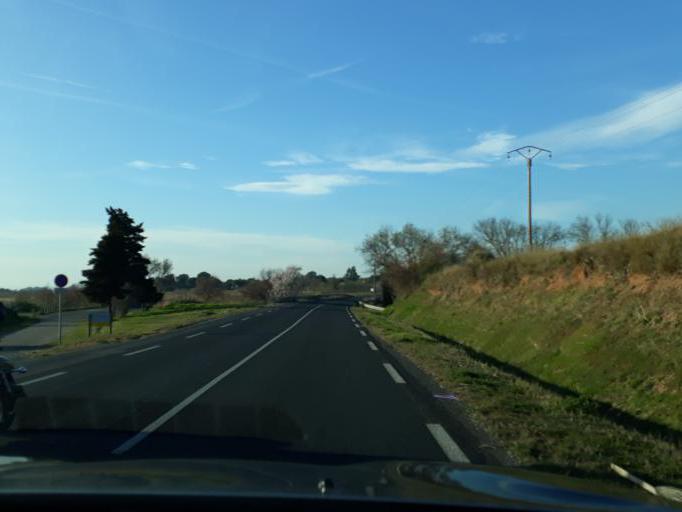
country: FR
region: Languedoc-Roussillon
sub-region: Departement de l'Herault
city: Marseillan
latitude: 43.3290
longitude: 3.5265
